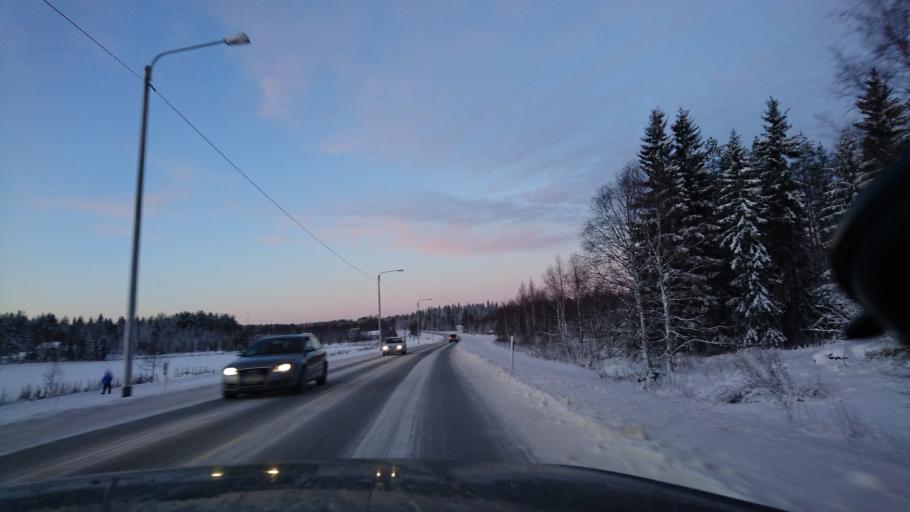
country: FI
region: Lapland
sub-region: Rovaniemi
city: Ranua
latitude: 65.9357
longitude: 26.4923
